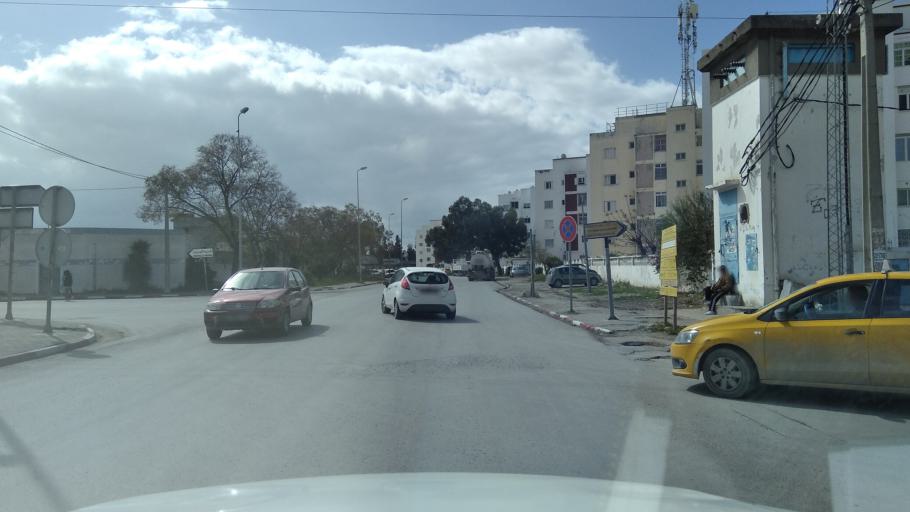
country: TN
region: Bin 'Arus
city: Ben Arous
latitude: 36.7444
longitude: 10.2261
